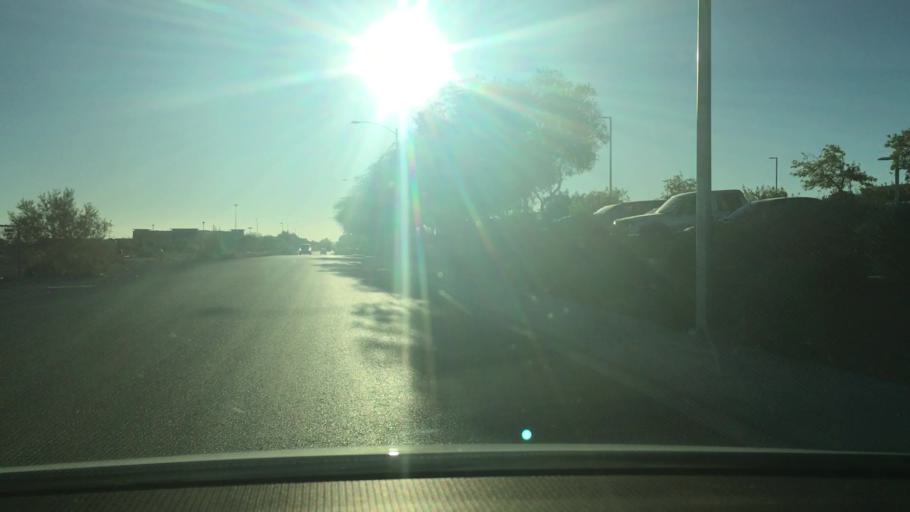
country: US
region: Nevada
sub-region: Clark County
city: Summerlin South
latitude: 36.0739
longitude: -115.2957
